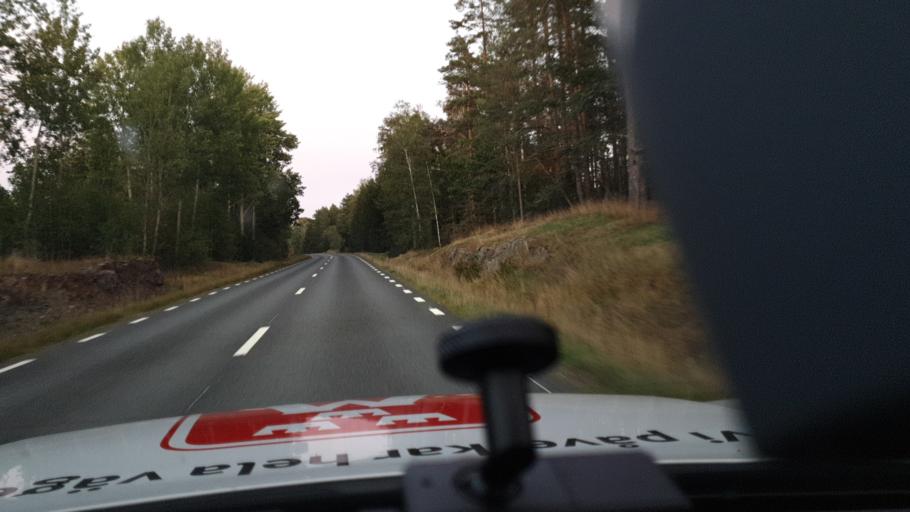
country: SE
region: Kalmar
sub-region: Hogsby Kommun
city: Hoegsby
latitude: 57.1146
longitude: 16.1548
